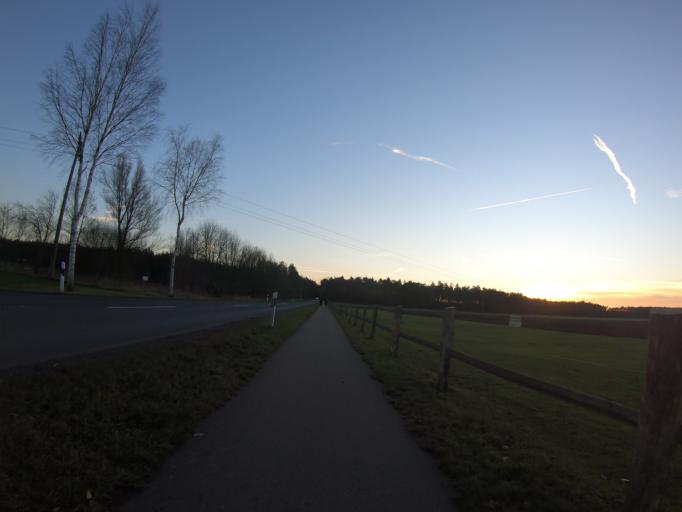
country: DE
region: Lower Saxony
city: Wagenhoff
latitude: 52.5059
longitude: 10.4818
